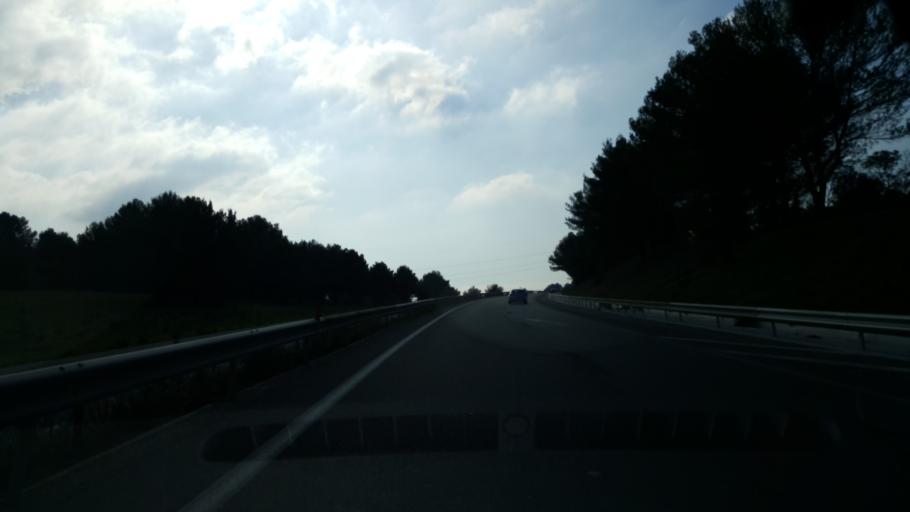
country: FR
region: Provence-Alpes-Cote d'Azur
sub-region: Departement des Bouches-du-Rhone
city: Auriol
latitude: 43.3558
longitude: 5.6250
